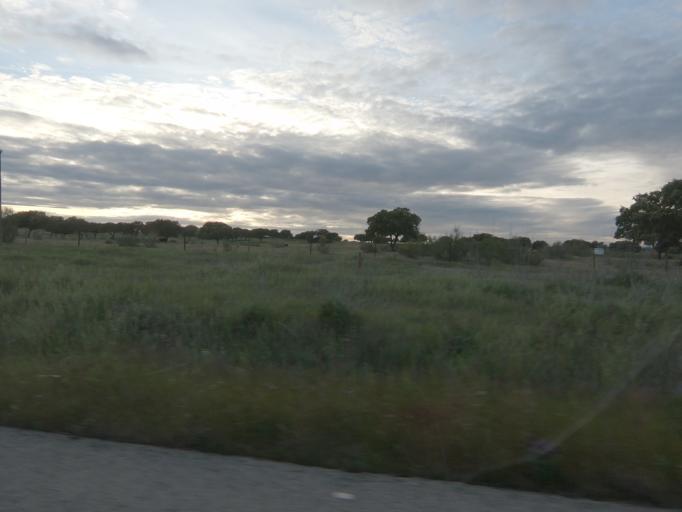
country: ES
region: Extremadura
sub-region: Provincia de Caceres
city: Malpartida de Caceres
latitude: 39.3676
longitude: -6.4582
